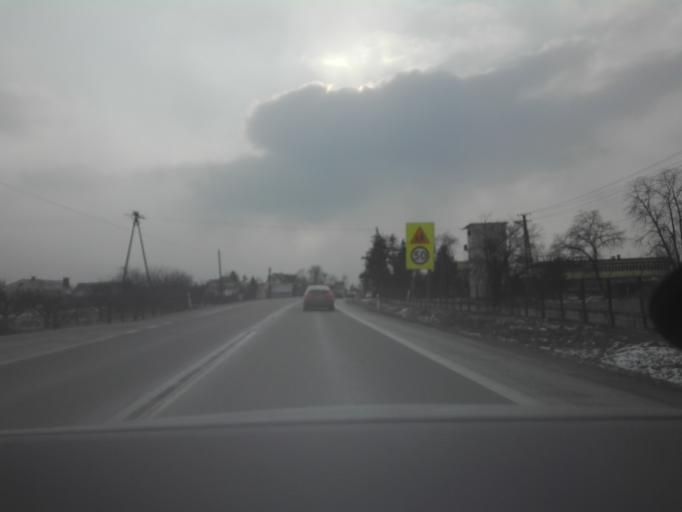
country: PL
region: Subcarpathian Voivodeship
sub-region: Powiat tarnobrzeski
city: Sokolniki
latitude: 50.6589
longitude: 21.7848
